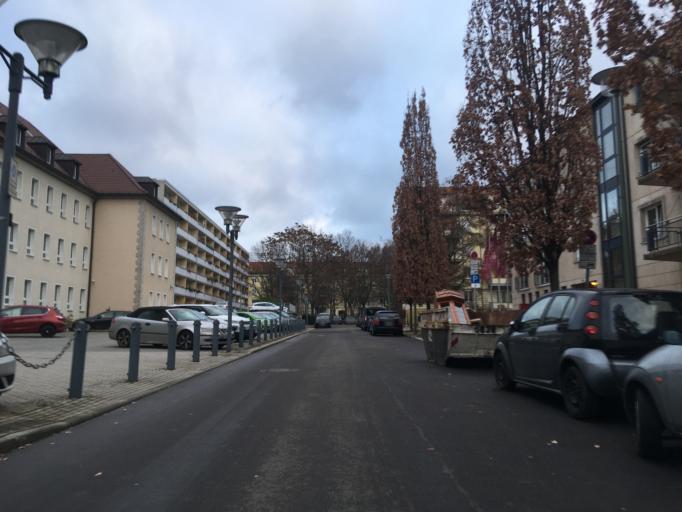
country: DE
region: Berlin
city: Prenzlauer Berg Bezirk
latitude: 52.5293
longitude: 13.4287
